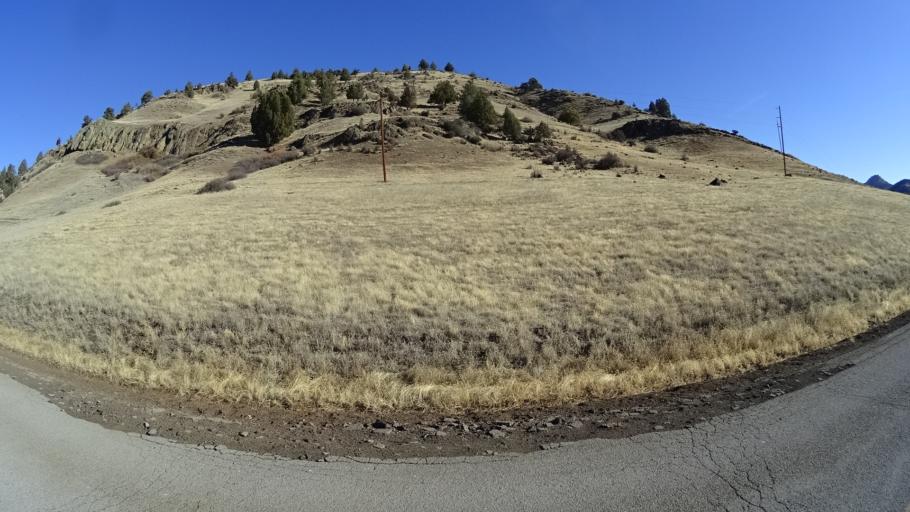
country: US
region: California
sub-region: Siskiyou County
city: Montague
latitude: 41.9687
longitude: -122.3930
